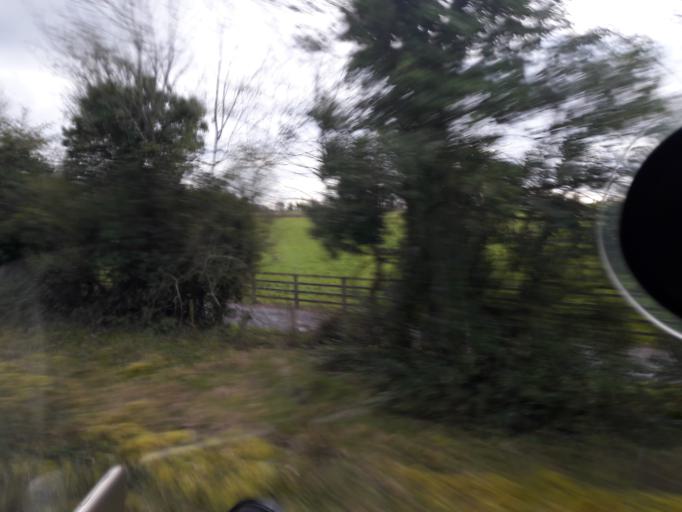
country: IE
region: Leinster
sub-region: An Iarmhi
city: An Muileann gCearr
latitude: 53.5986
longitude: -7.3943
